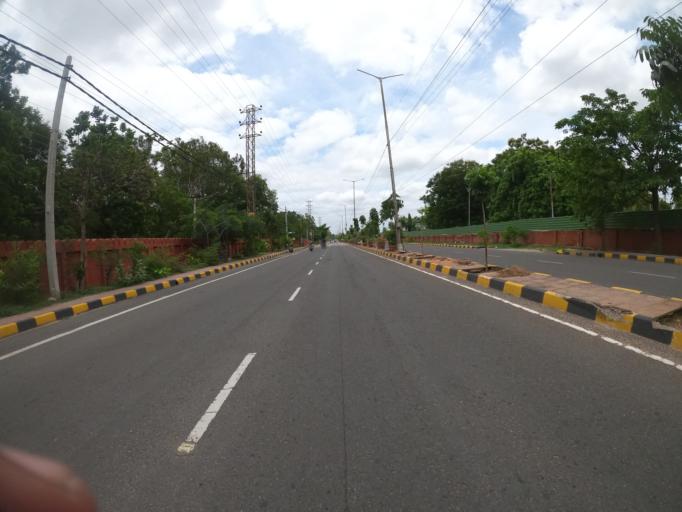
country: IN
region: Telangana
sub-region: Hyderabad
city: Hyderabad
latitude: 17.3744
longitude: 78.4000
